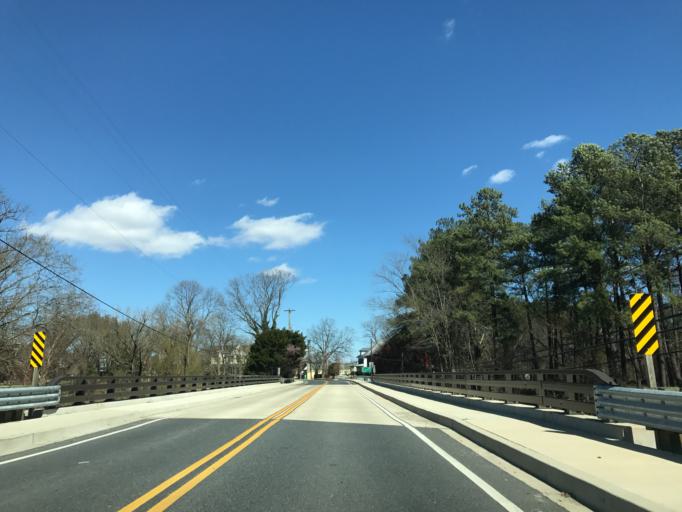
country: US
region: Delaware
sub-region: New Castle County
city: Townsend
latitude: 39.2565
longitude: -75.8396
